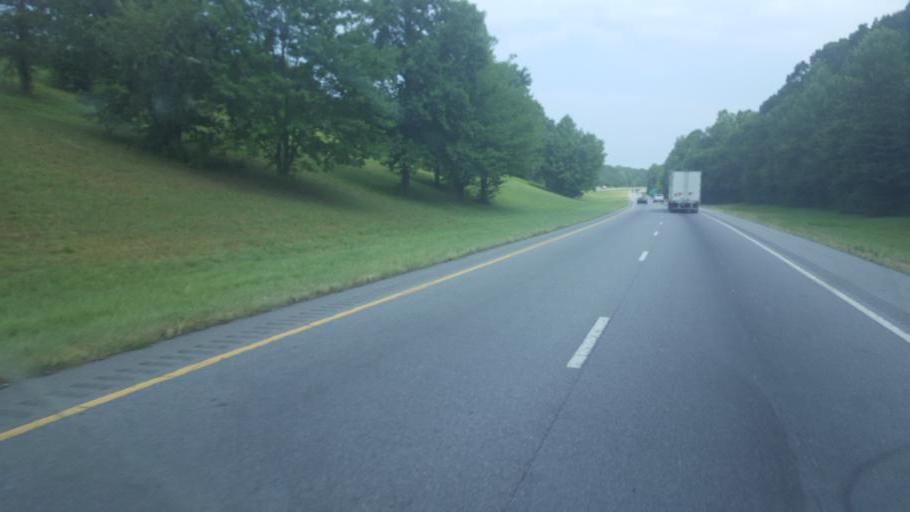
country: US
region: North Carolina
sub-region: Iredell County
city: Statesville
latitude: 35.9812
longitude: -80.8377
